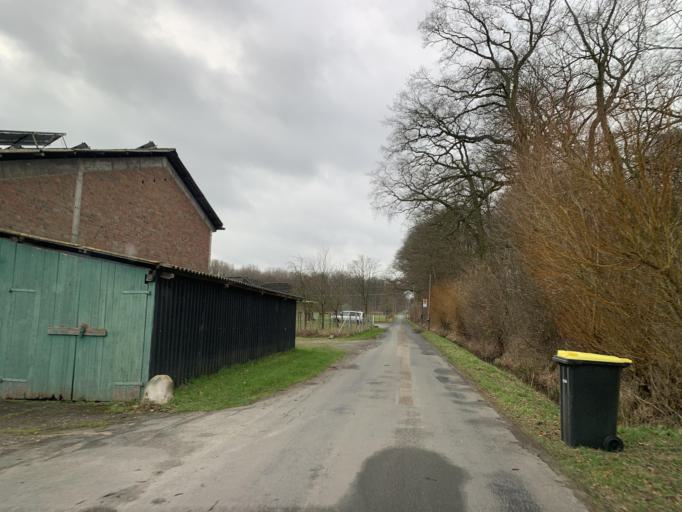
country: DE
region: North Rhine-Westphalia
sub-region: Regierungsbezirk Munster
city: Dulmen
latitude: 51.8462
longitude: 7.3207
